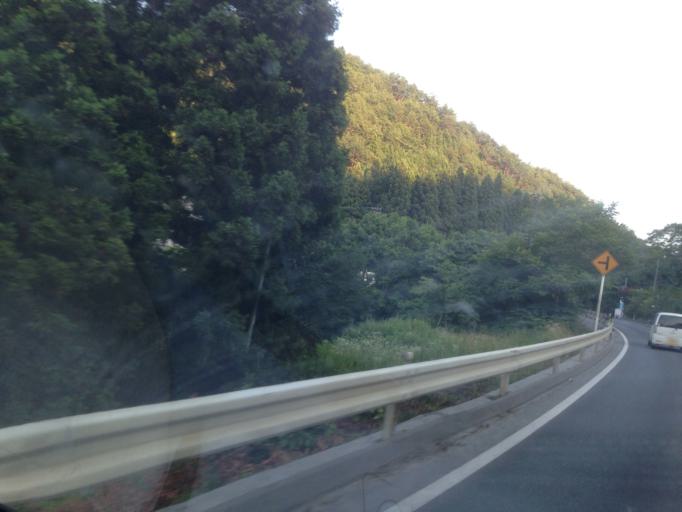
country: JP
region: Iwate
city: Kamaishi
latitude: 39.3174
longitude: 141.8835
